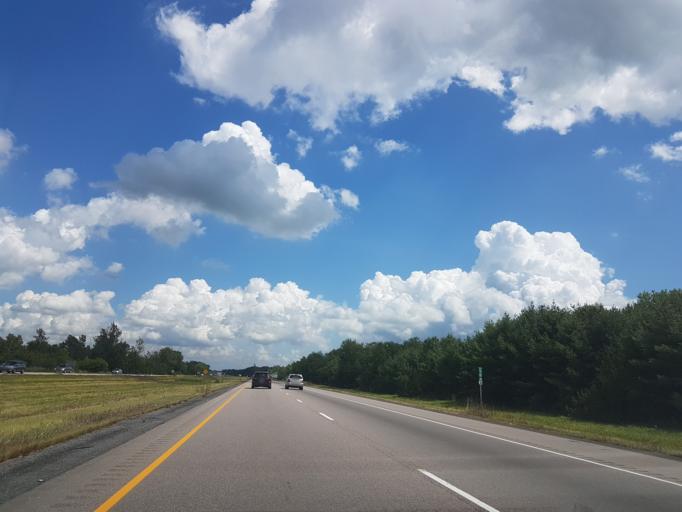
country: CA
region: Ontario
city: Skatepark
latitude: 44.2727
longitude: -76.9019
